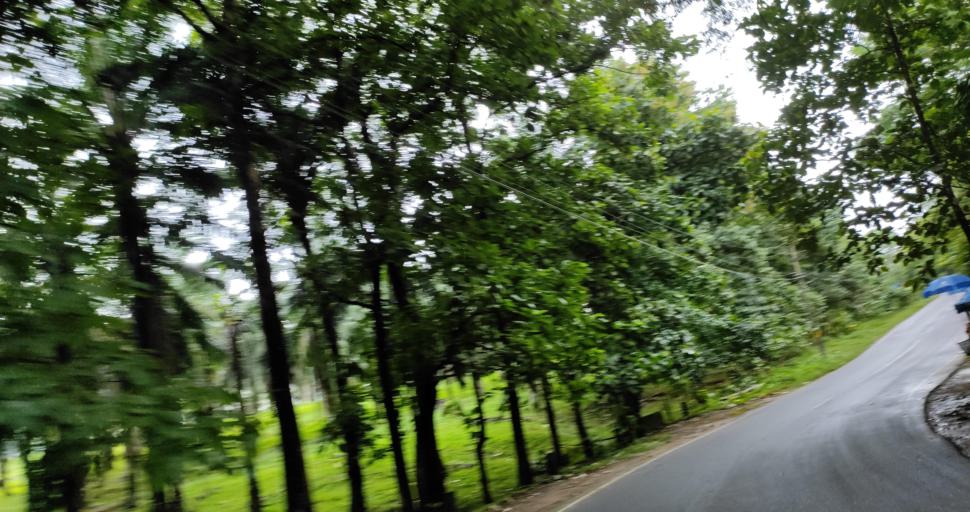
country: IN
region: Kerala
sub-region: Ernakulam
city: Angamali
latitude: 10.2879
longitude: 76.5526
